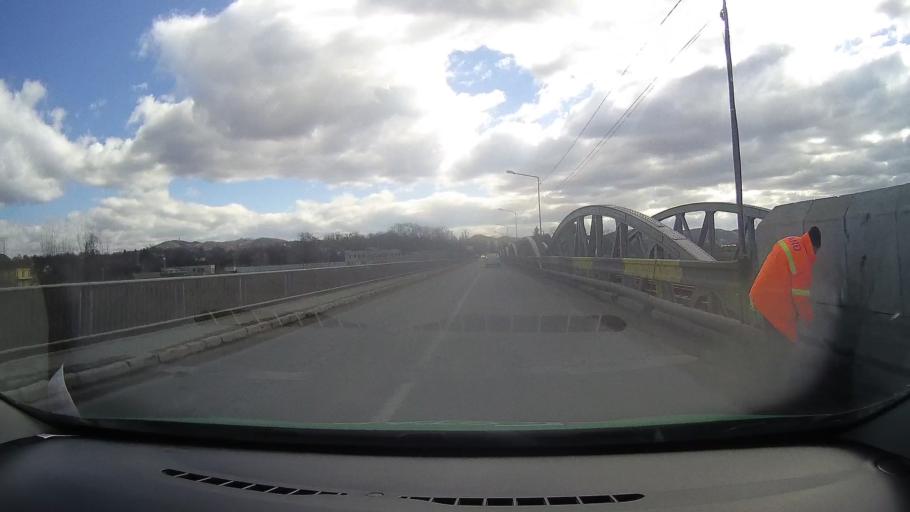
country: RO
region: Dambovita
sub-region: Oras Pucioasa
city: Pucioasa
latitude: 45.0823
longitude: 25.4238
